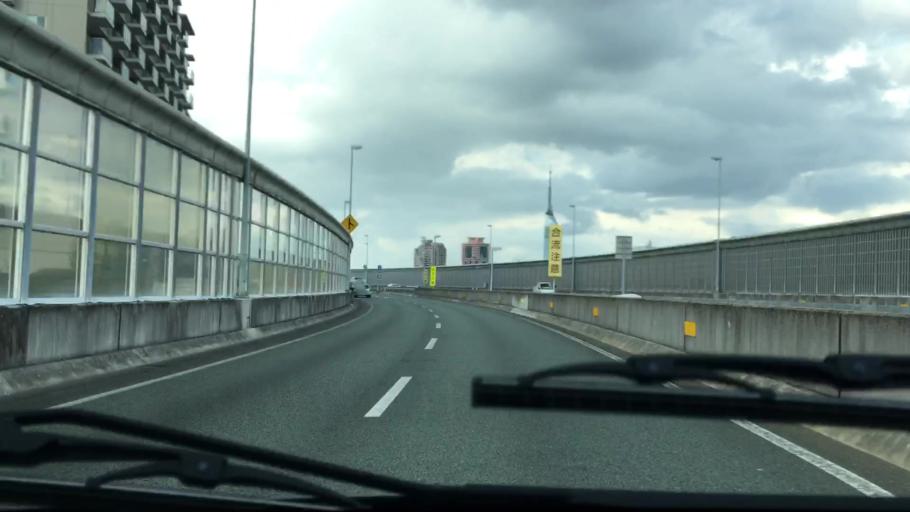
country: JP
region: Fukuoka
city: Fukuoka-shi
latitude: 33.5838
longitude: 130.3395
